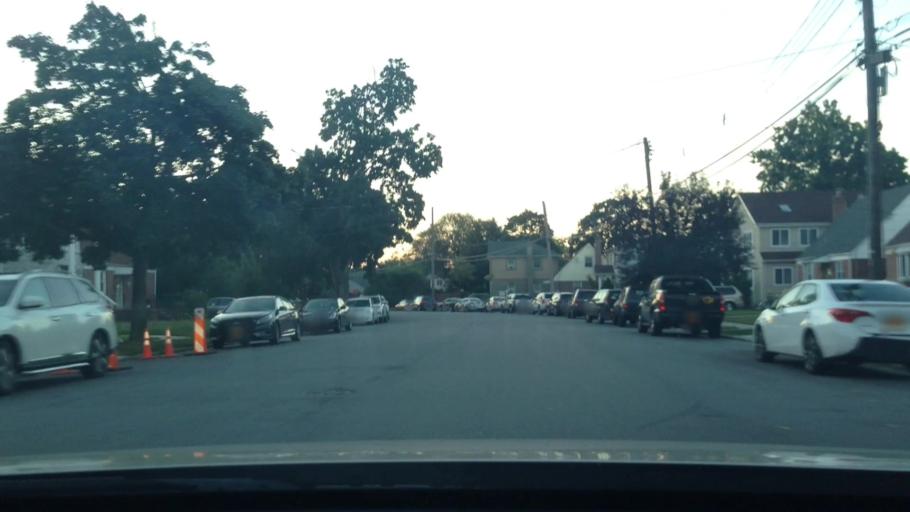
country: US
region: New York
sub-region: Nassau County
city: North New Hyde Park
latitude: 40.7541
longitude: -73.7053
